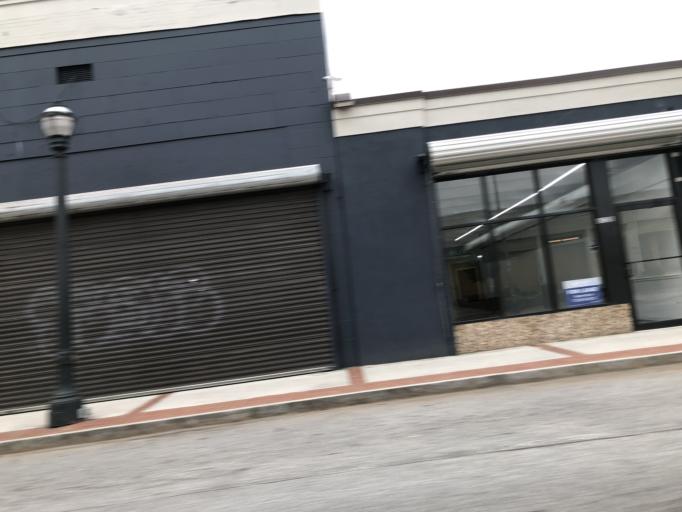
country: US
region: Georgia
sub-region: Fulton County
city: Atlanta
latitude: 33.7382
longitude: -84.4155
